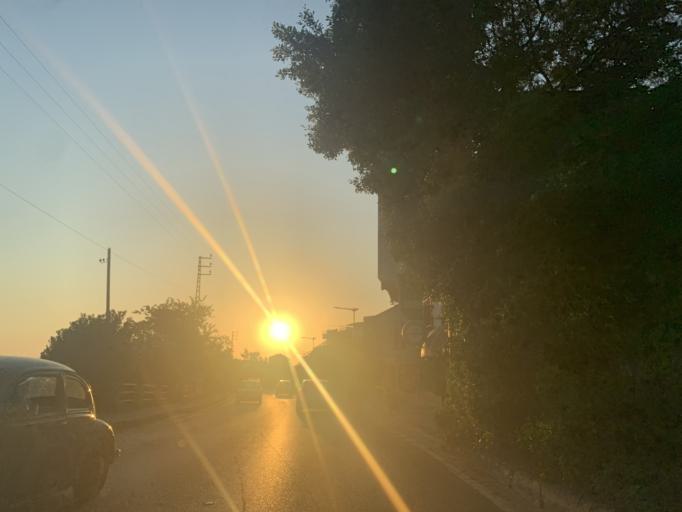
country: LB
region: Mont-Liban
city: Djounie
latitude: 33.9613
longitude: 35.6253
